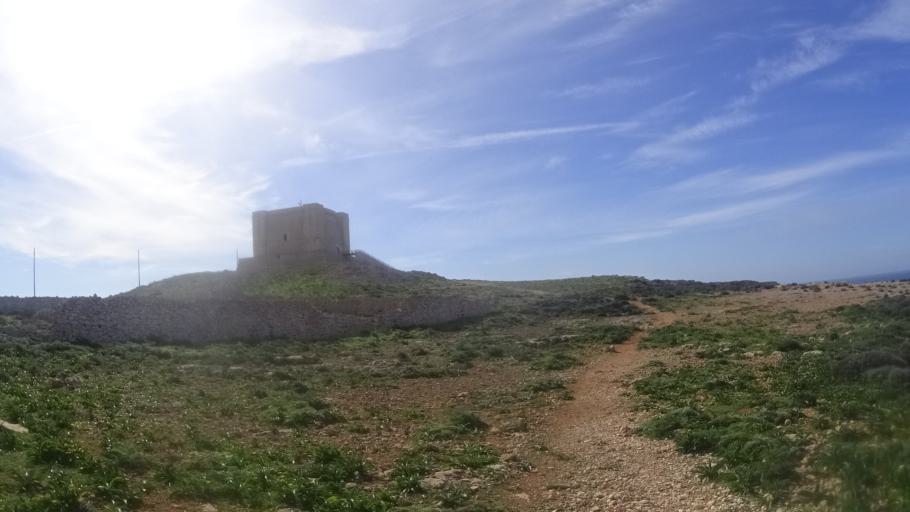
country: MT
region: Il-Qala
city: Qala
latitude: 36.0082
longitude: 14.3297
